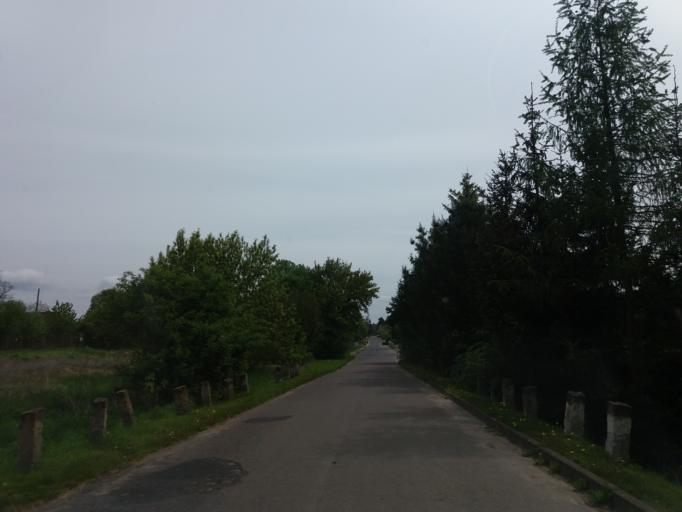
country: PL
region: Lubusz
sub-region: Powiat strzelecko-drezdenecki
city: Dobiegniew
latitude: 52.9715
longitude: 15.7410
